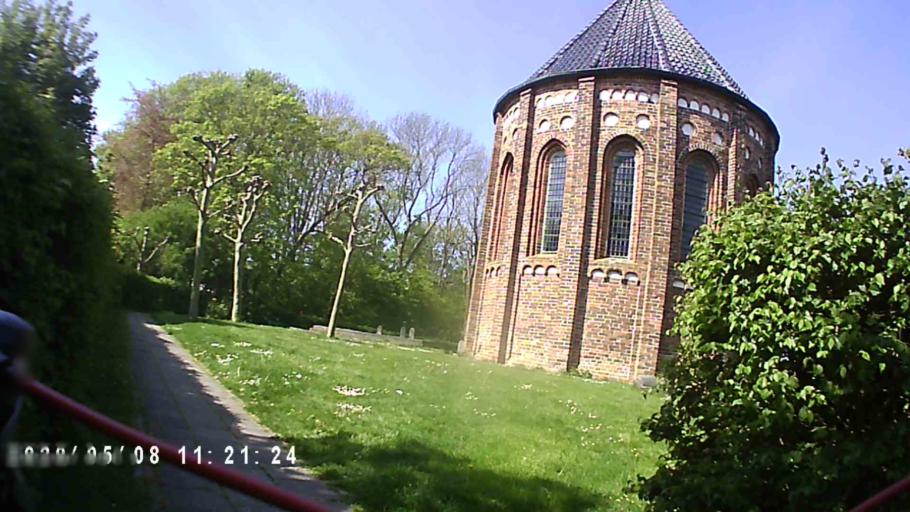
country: NL
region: Groningen
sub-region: Gemeente Bedum
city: Bedum
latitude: 53.3453
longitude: 6.6737
